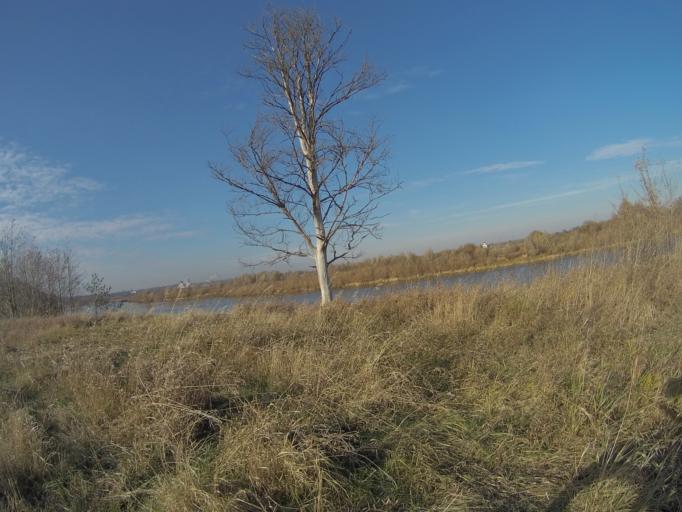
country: RU
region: Vladimir
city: Bogolyubovo
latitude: 56.1833
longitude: 40.5617
